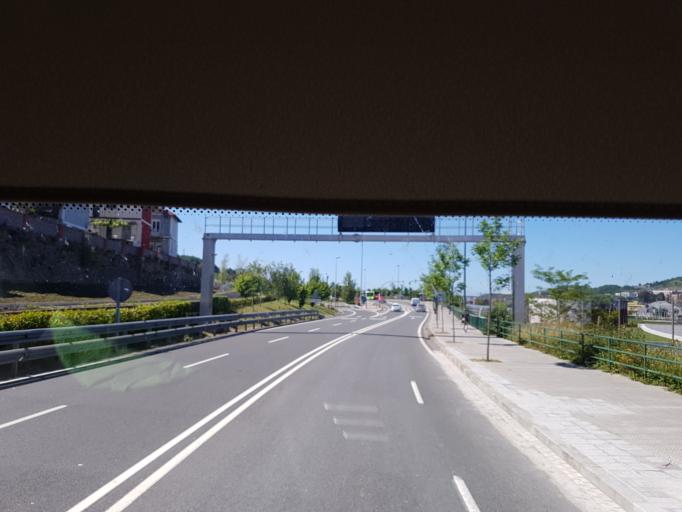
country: ES
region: Basque Country
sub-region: Bizkaia
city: Bilbao
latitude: 43.2614
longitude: -2.9556
